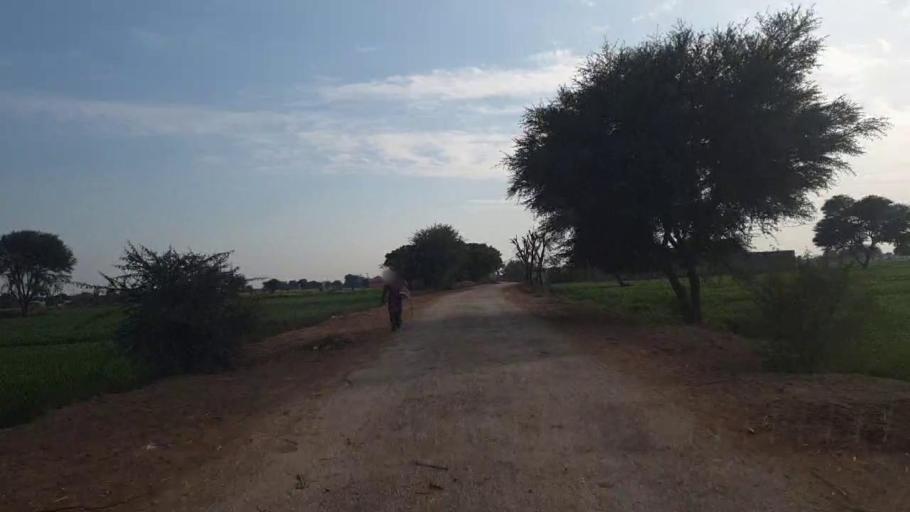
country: PK
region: Sindh
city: Shahpur Chakar
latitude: 26.0496
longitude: 68.5645
